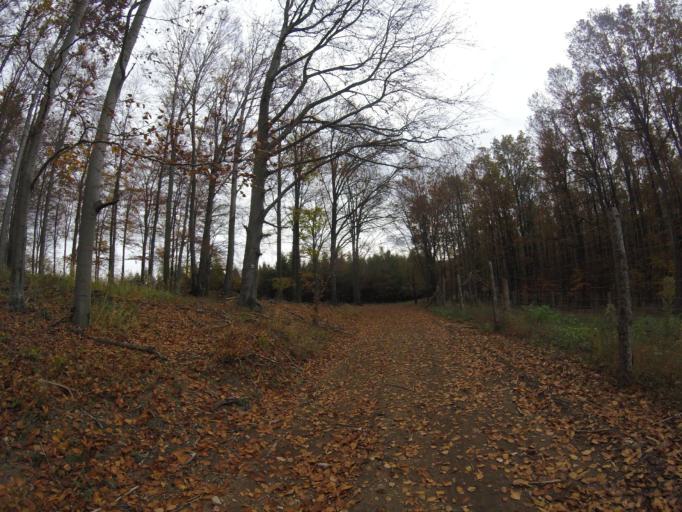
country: HU
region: Borsod-Abauj-Zemplen
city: Gonc
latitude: 48.4123
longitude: 21.3834
